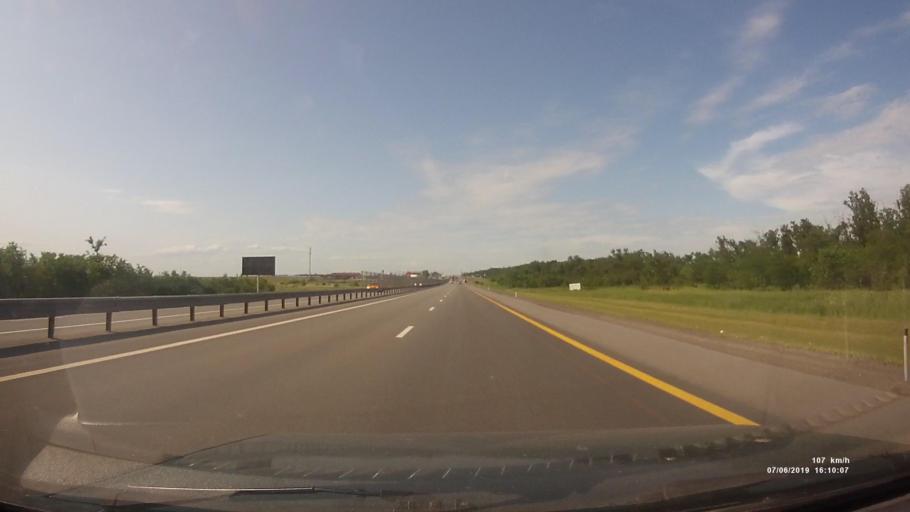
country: RU
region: Rostov
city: Likhoy
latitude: 48.0933
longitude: 40.2601
